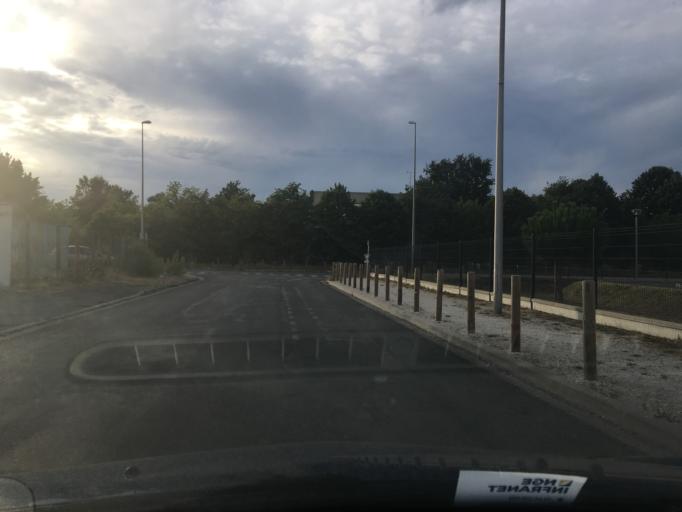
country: FR
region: Aquitaine
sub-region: Departement de la Gironde
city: Canejan
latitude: 44.7812
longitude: -0.6541
